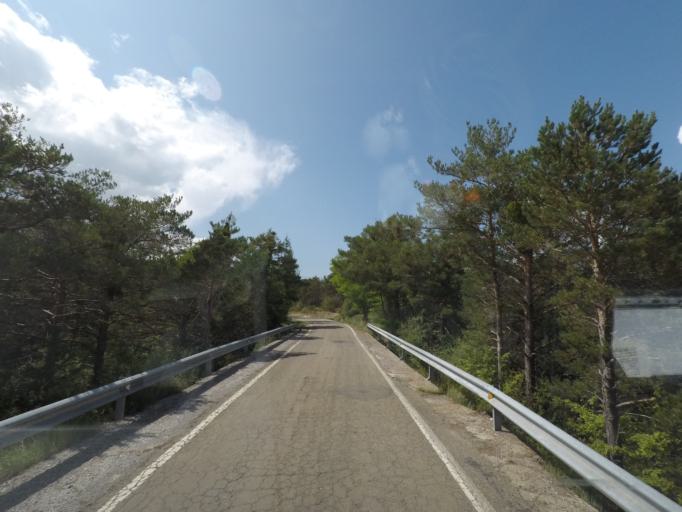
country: ES
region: Aragon
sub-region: Provincia de Huesca
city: Yebra de Basa
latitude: 42.4025
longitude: -0.3593
